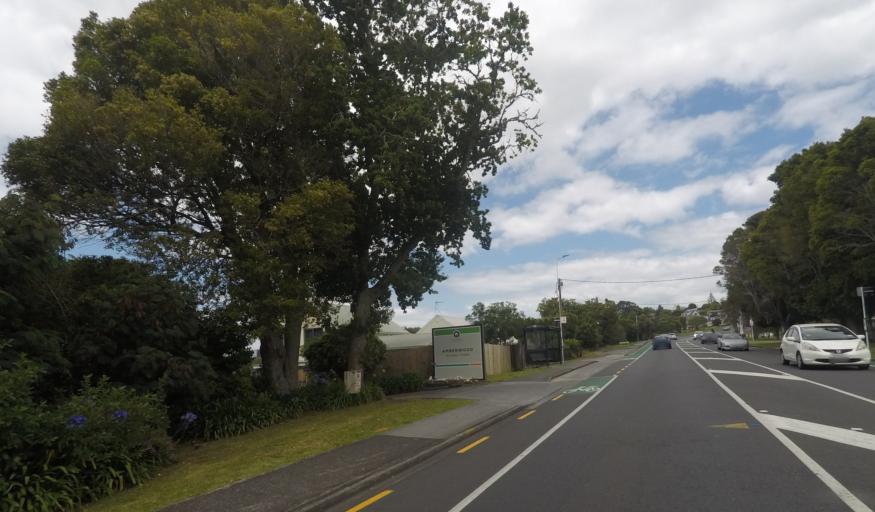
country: NZ
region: Auckland
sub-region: Auckland
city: Rosebank
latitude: -36.8269
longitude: 174.6078
